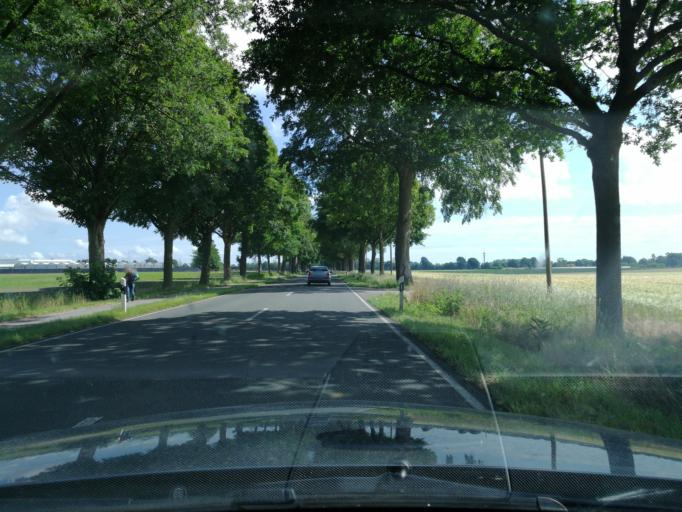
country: DE
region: North Rhine-Westphalia
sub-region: Regierungsbezirk Dusseldorf
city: Kleve
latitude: 51.7491
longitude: 6.0918
